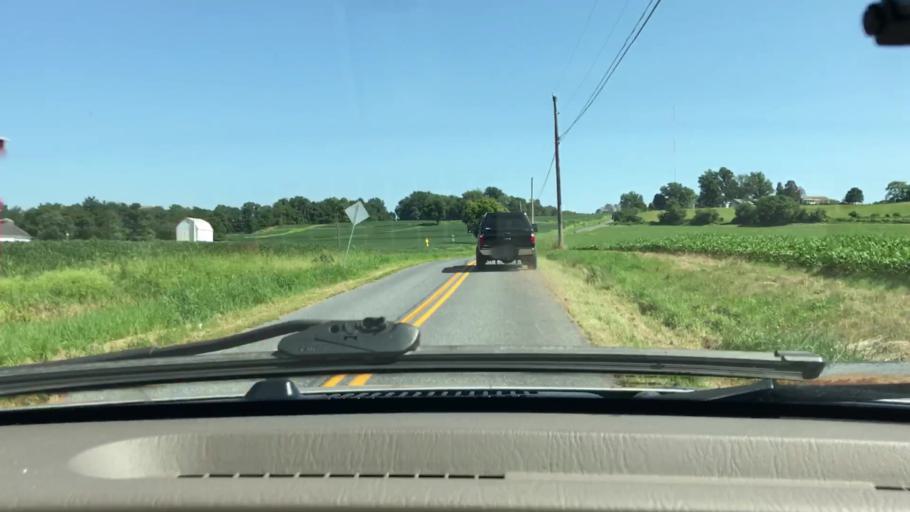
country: US
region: Pennsylvania
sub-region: Lancaster County
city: Elizabethtown
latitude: 40.1819
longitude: -76.6106
